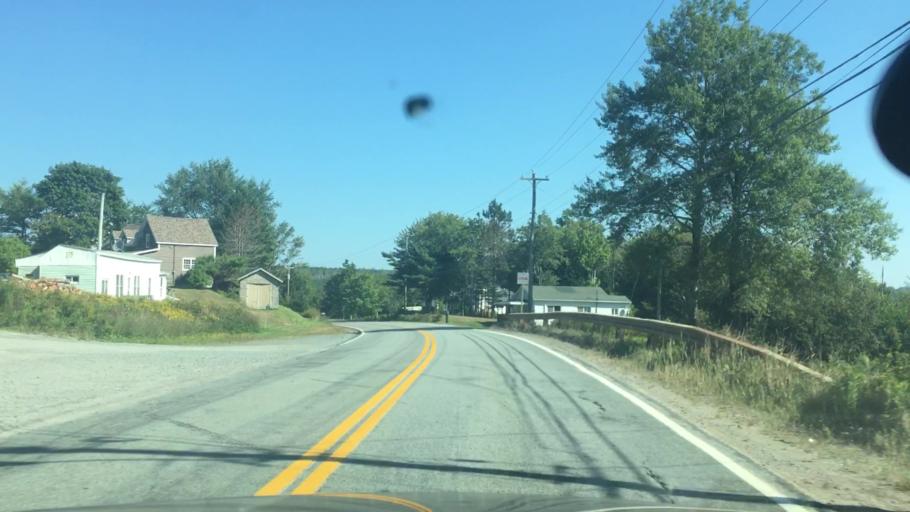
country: CA
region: Nova Scotia
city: New Glasgow
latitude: 44.9135
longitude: -62.5395
